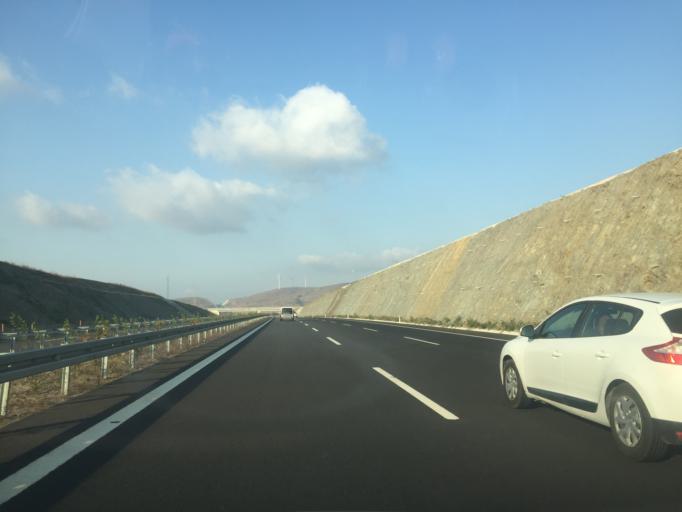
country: TR
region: Balikesir
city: Ertugrul
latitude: 39.6820
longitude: 27.7590
